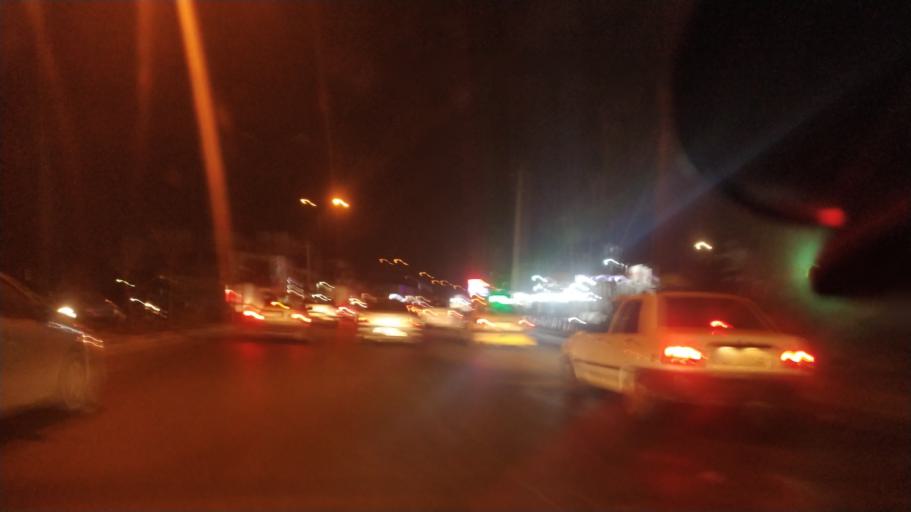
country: IR
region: Alborz
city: Karaj
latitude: 35.7846
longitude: 51.0061
